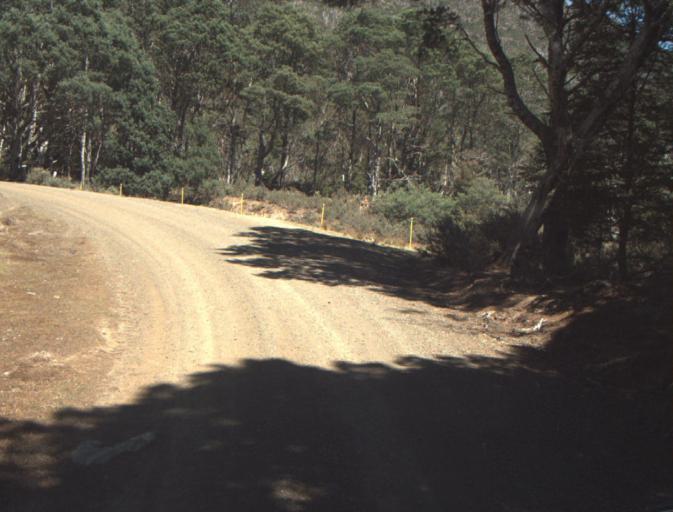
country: AU
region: Tasmania
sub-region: Dorset
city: Scottsdale
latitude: -41.3653
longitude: 147.4303
